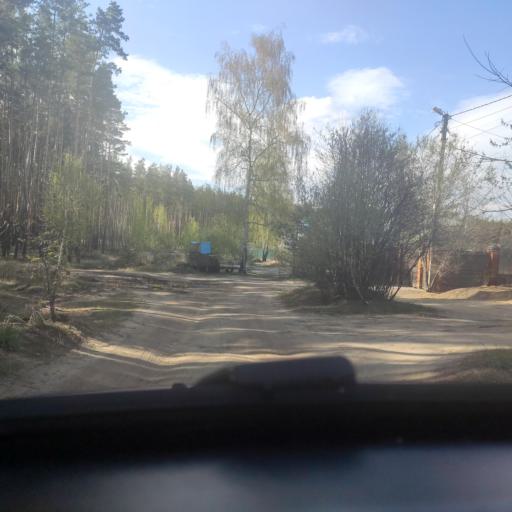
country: RU
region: Voronezj
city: Somovo
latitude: 51.7525
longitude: 39.3215
